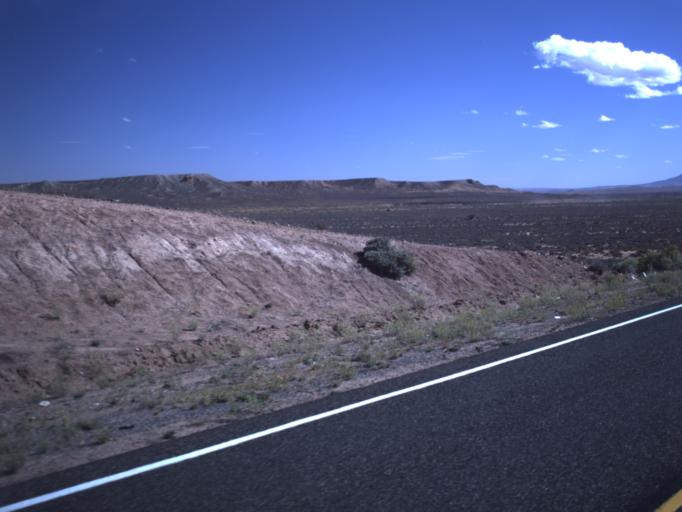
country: US
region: Utah
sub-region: Wayne County
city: Loa
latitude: 38.1135
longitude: -110.6243
